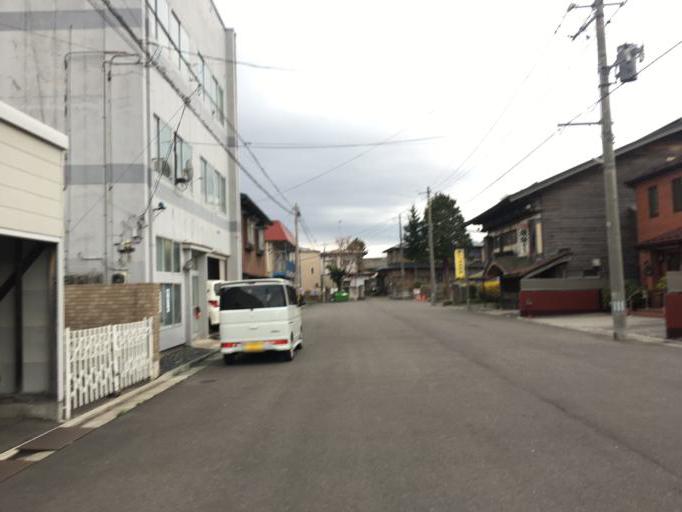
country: JP
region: Aomori
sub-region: Hachinohe Shi
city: Uchimaru
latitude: 40.5200
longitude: 141.5184
